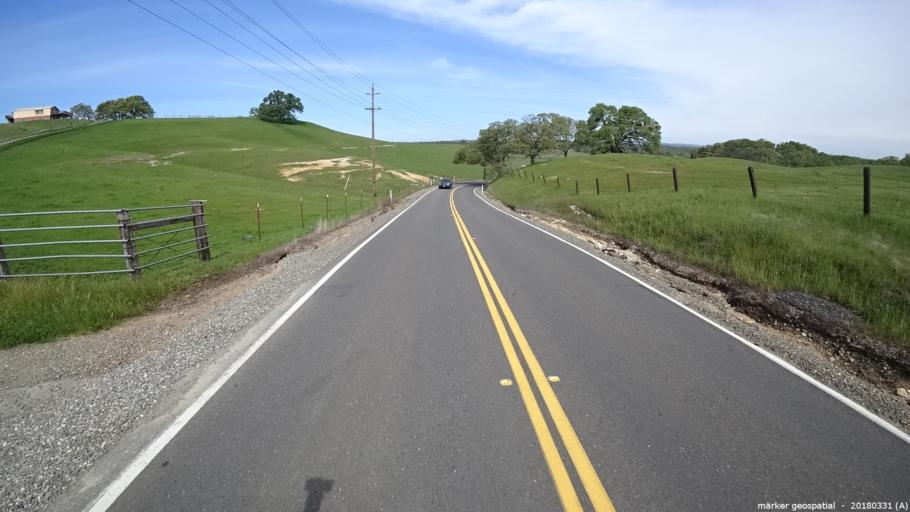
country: US
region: California
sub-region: Sacramento County
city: Rancho Murieta
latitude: 38.5158
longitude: -121.1020
